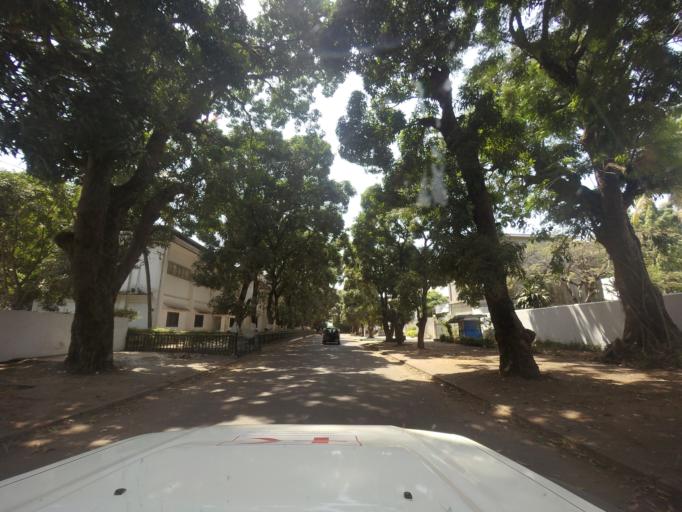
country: GN
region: Conakry
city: Camayenne
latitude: 9.5066
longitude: -13.7171
